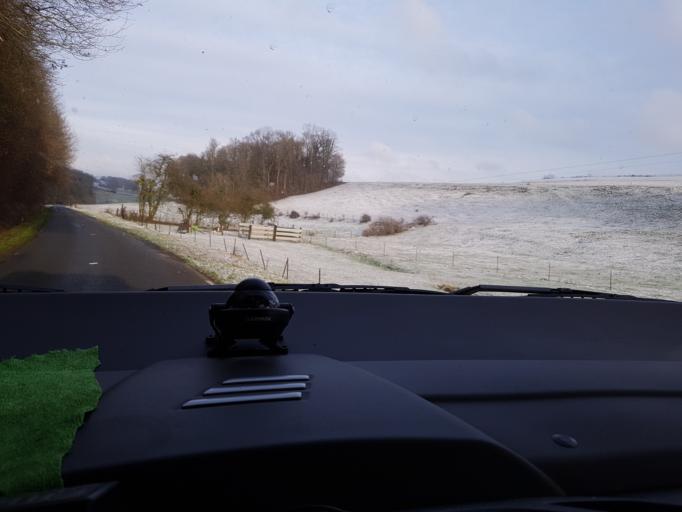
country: FR
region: Champagne-Ardenne
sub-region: Departement des Ardennes
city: Tournes
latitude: 49.7360
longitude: 4.5774
